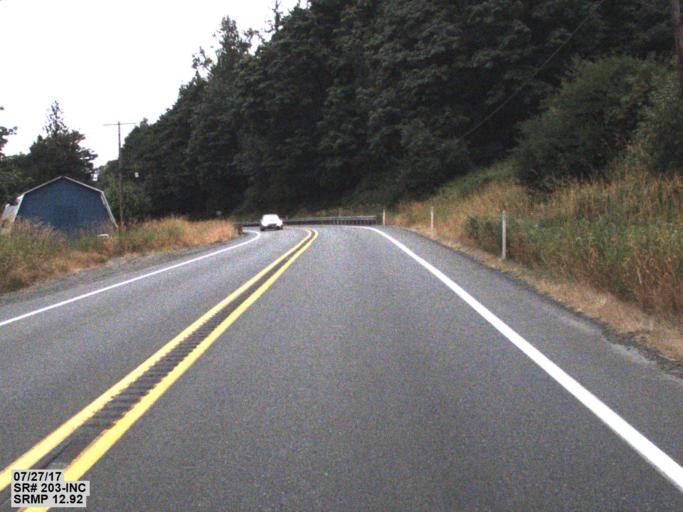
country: US
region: Washington
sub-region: King County
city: Duvall
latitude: 47.7132
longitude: -121.9843
